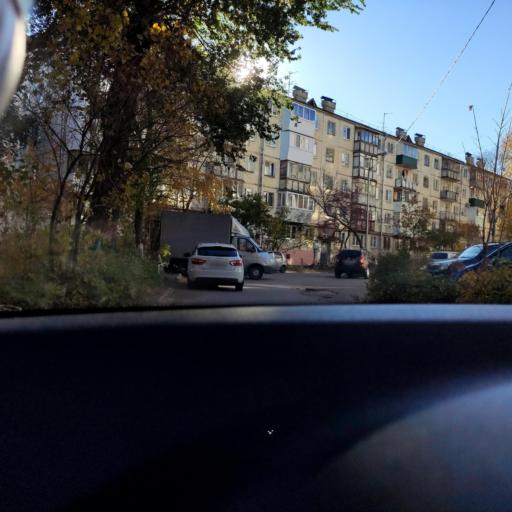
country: RU
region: Samara
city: Samara
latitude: 53.1908
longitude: 50.2038
